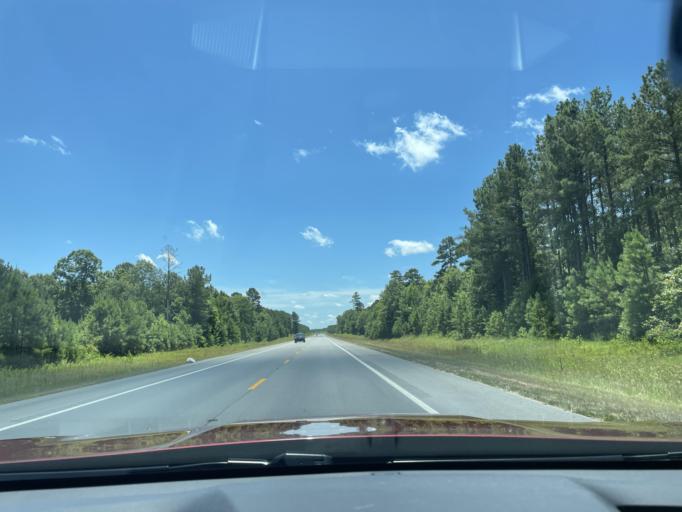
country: US
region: Arkansas
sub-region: Lincoln County
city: Star City
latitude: 33.9710
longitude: -91.9152
